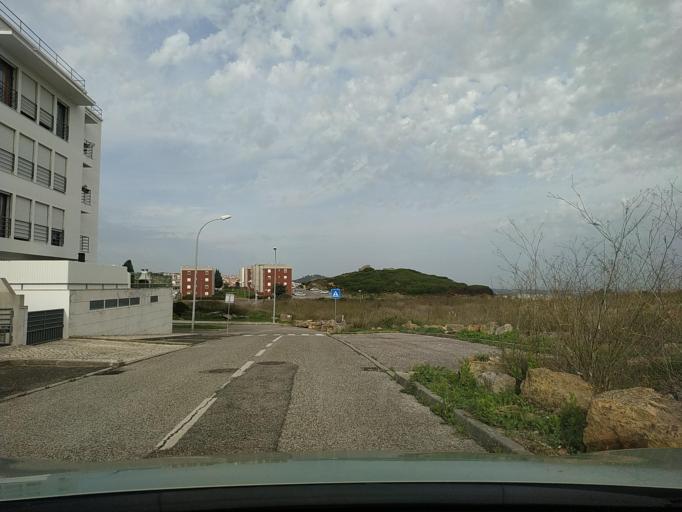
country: PT
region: Lisbon
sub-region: Odivelas
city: Famoes
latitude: 38.7834
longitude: -9.2316
